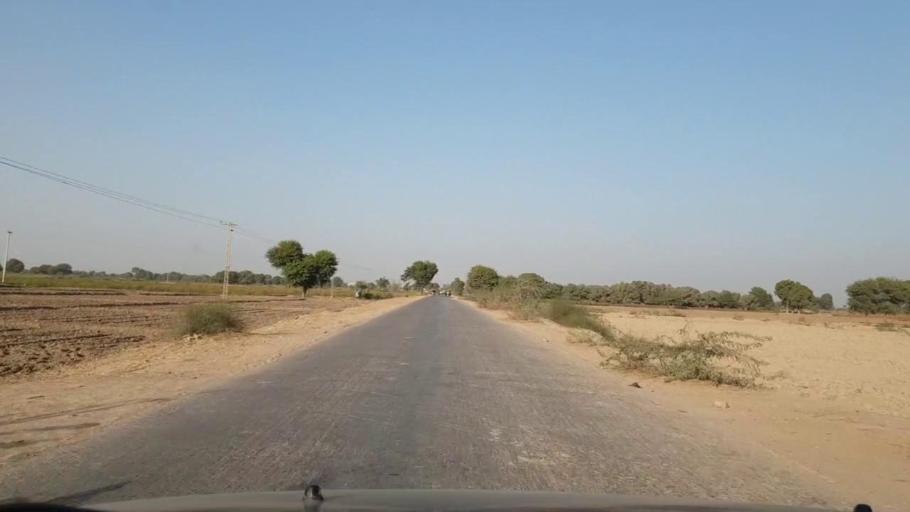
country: PK
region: Sindh
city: Chambar
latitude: 25.2329
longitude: 68.7835
